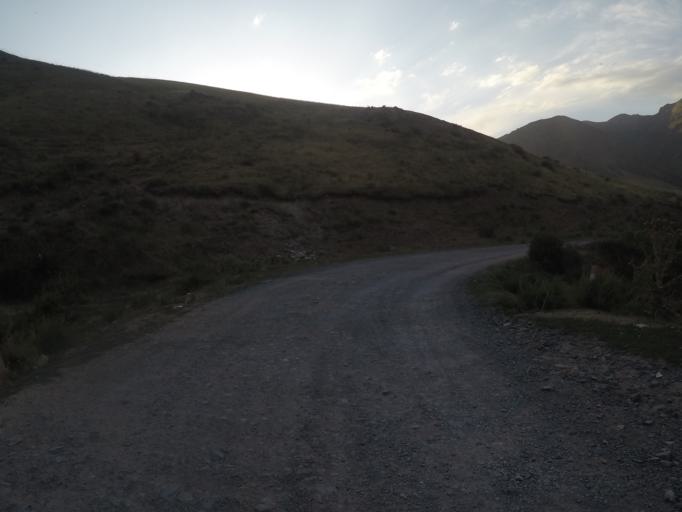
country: KG
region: Chuy
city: Bishkek
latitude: 42.6646
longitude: 74.6479
